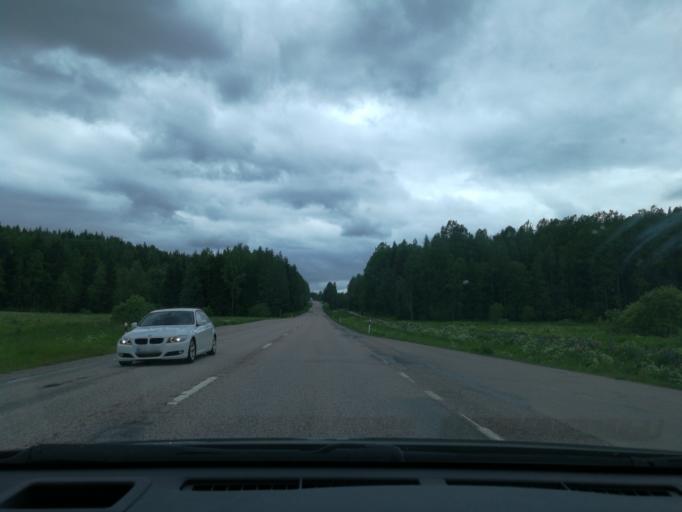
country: SE
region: Vaestmanland
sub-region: Fagersta Kommun
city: Fagersta
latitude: 59.9716
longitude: 15.7785
